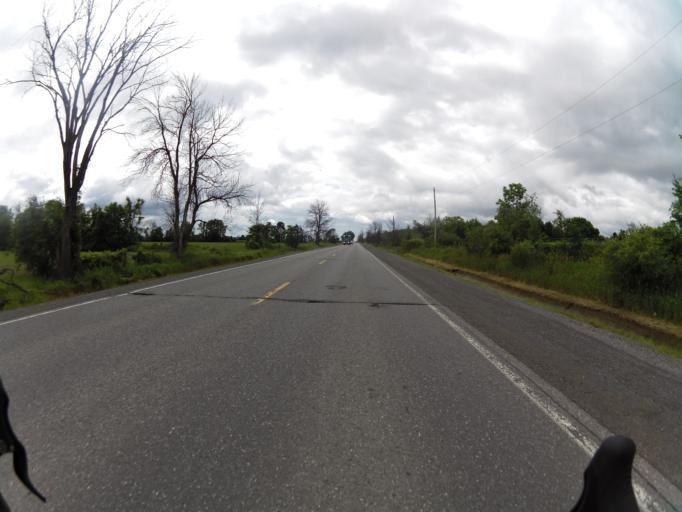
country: CA
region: Ontario
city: Bells Corners
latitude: 45.2653
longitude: -75.8555
